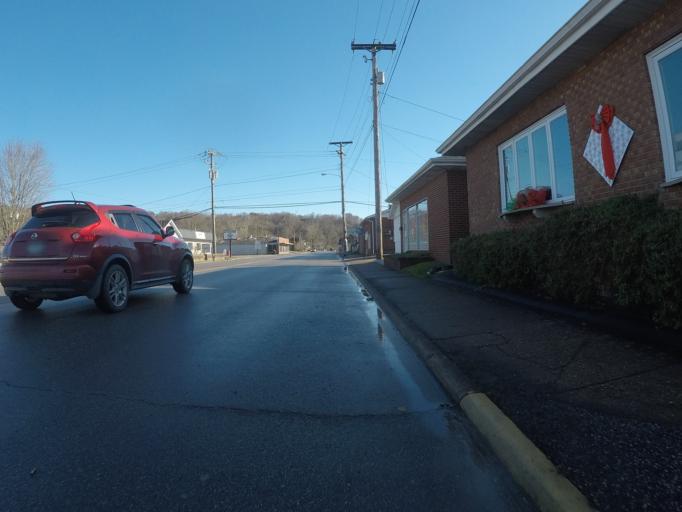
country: US
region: West Virginia
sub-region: Cabell County
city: Huntington
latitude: 38.4278
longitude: -82.4573
